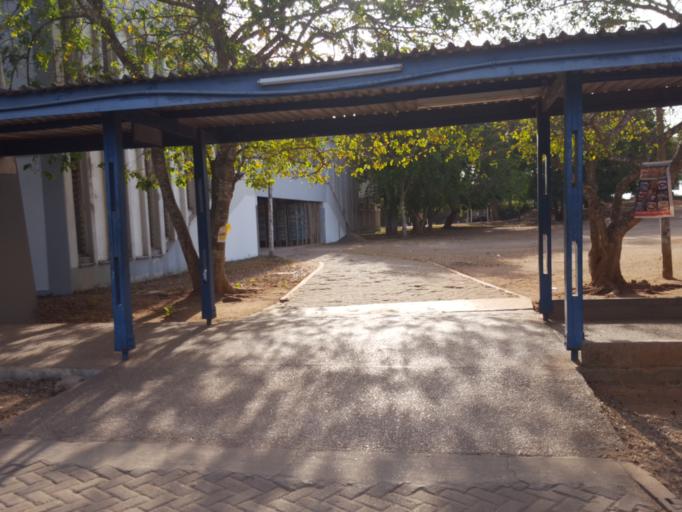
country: GH
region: Central
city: Cape Coast
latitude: 5.1172
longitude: -1.2929
